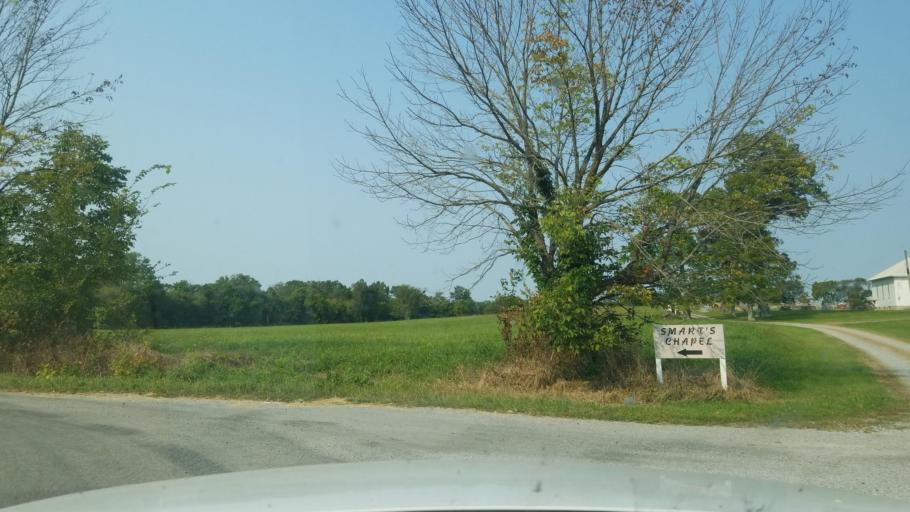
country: US
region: Illinois
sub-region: Saline County
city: Carrier Mills
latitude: 37.7942
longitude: -88.6608
